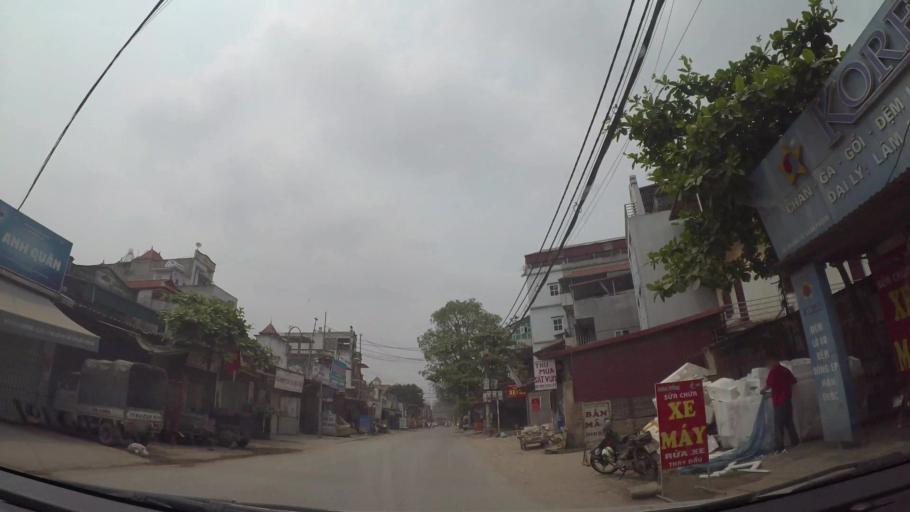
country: VN
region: Ha Noi
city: Cau Dien
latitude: 21.0334
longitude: 105.7389
